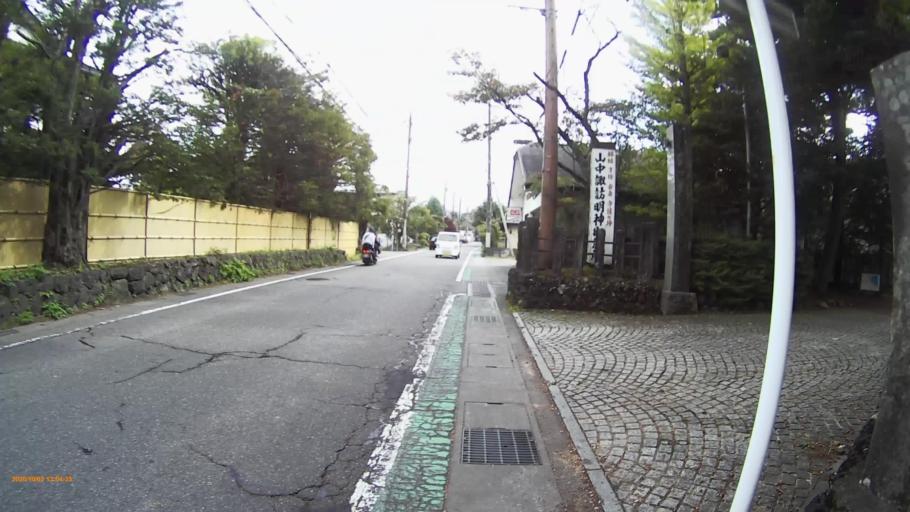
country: JP
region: Shizuoka
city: Gotemba
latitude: 35.4204
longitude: 138.8513
